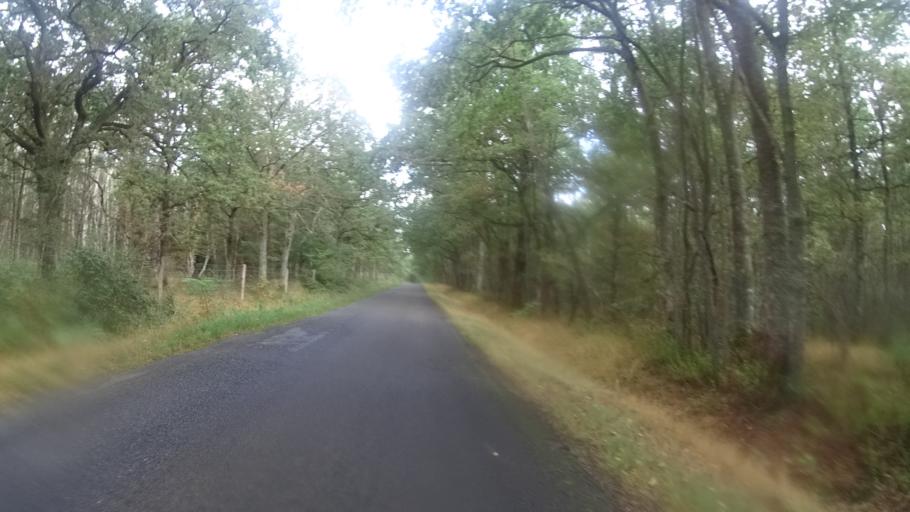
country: FR
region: Centre
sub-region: Departement du Loiret
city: Chateauneuf-sur-Loire
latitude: 47.9074
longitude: 2.2072
